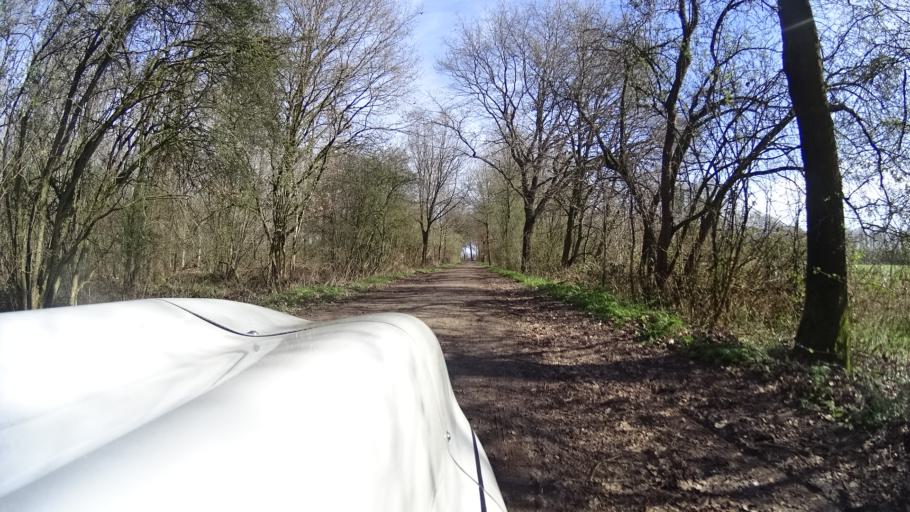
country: NL
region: North Brabant
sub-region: Gemeente Grave
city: Grave
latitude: 51.7187
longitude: 5.7856
